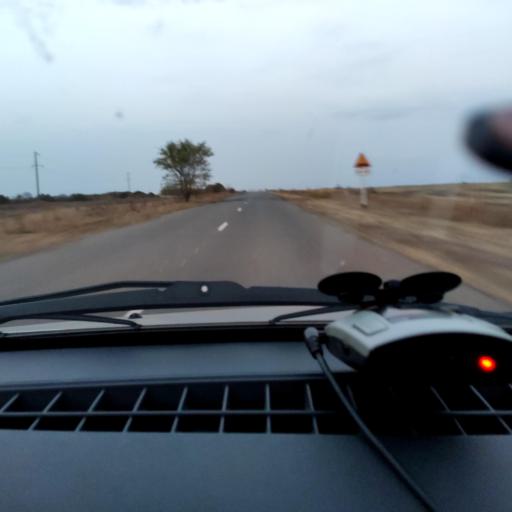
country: RU
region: Voronezj
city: Uryv-Pokrovka
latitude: 51.2408
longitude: 38.9697
